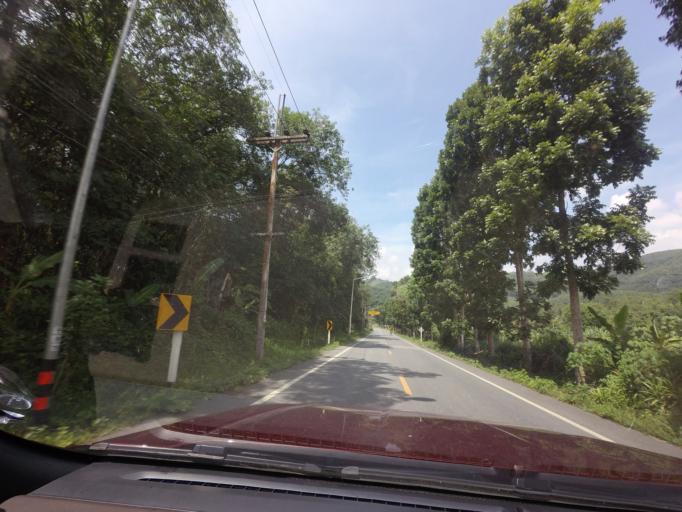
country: TH
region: Yala
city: Betong
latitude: 5.8411
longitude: 101.0742
